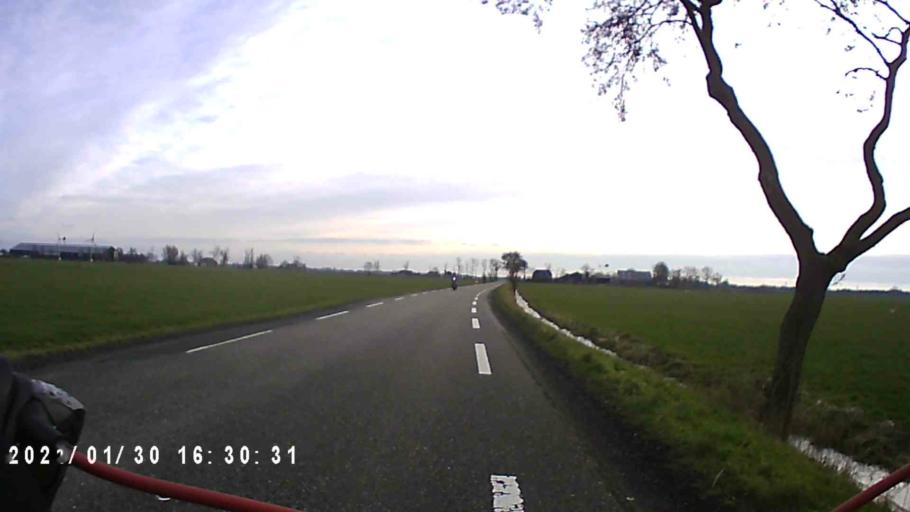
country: NL
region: Groningen
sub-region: Gemeente Zuidhorn
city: Zuidhorn
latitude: 53.2196
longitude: 6.3877
